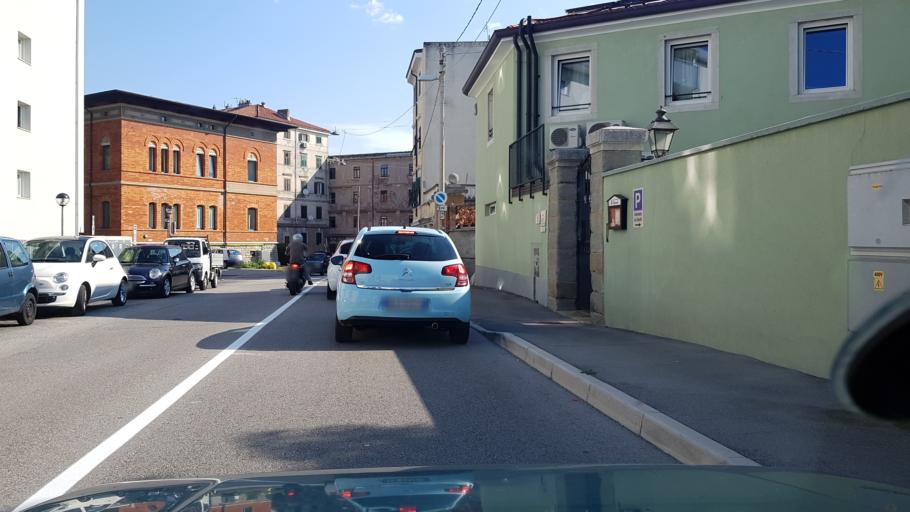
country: IT
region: Friuli Venezia Giulia
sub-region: Provincia di Trieste
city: Trieste
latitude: 45.6367
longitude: 13.7873
